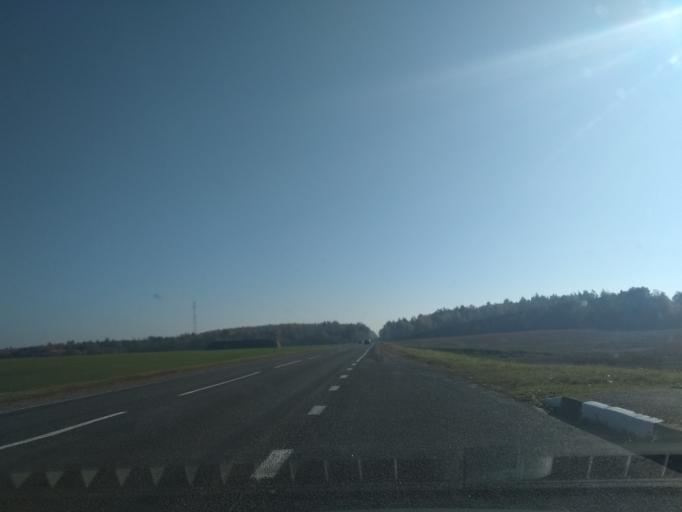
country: BY
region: Grodnenskaya
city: Slonim
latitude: 53.1133
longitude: 25.1556
